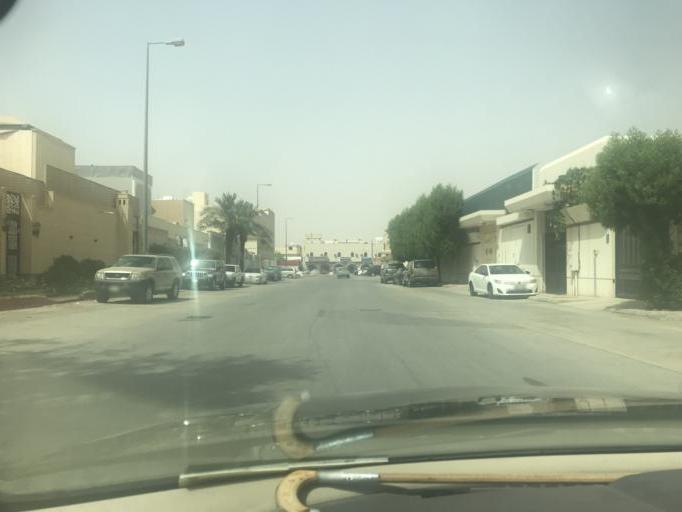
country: SA
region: Ar Riyad
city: Riyadh
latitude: 24.7451
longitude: 46.7878
